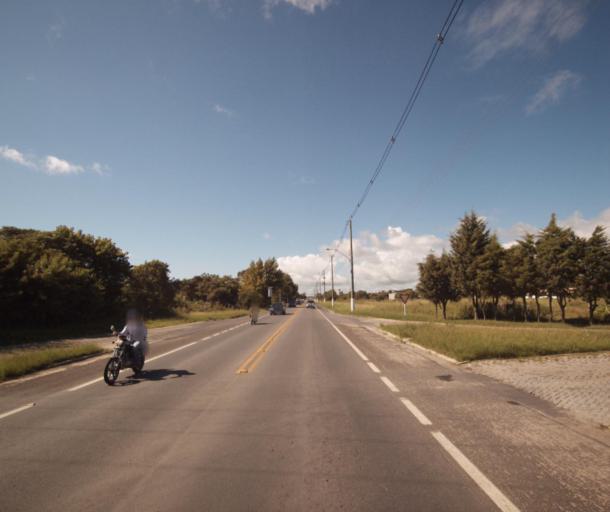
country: BR
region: Rio Grande do Sul
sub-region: Pelotas
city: Pelotas
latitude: -31.7534
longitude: -52.3586
